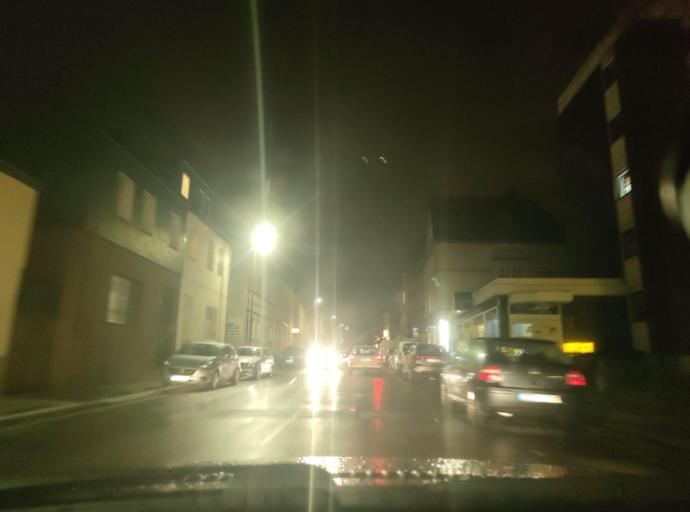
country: DE
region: North Rhine-Westphalia
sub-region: Regierungsbezirk Dusseldorf
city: Essen
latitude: 51.4844
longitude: 7.0636
